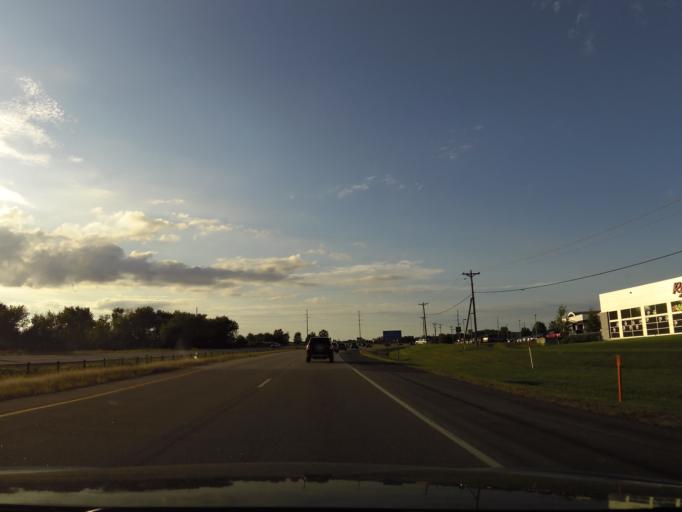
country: US
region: Minnesota
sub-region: Dakota County
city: Hastings
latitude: 44.7685
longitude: -92.8610
